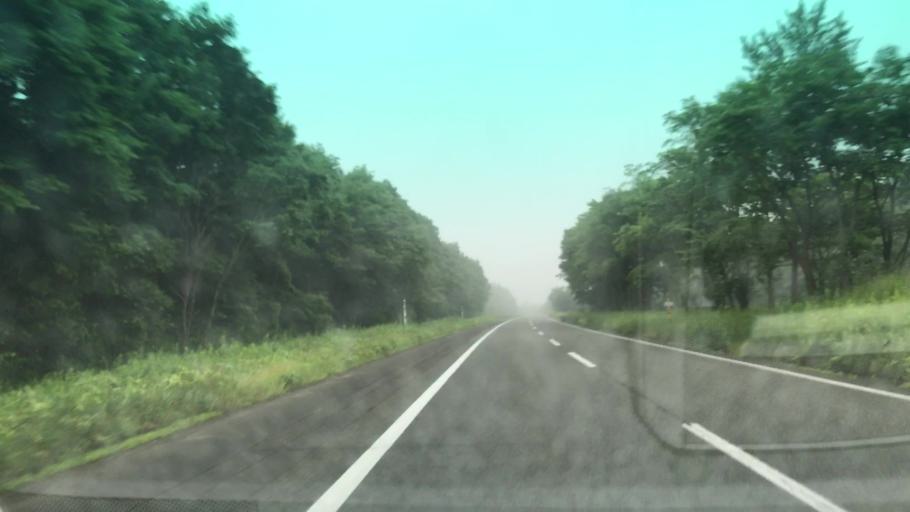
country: JP
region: Hokkaido
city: Chitose
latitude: 42.7923
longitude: 141.6270
